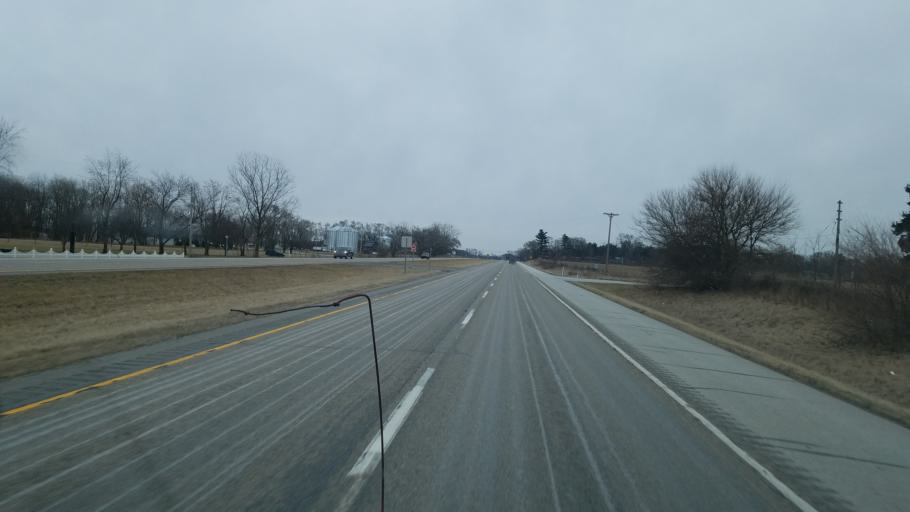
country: US
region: Indiana
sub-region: LaPorte County
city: Kingsford Heights
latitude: 41.4198
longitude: -86.7854
